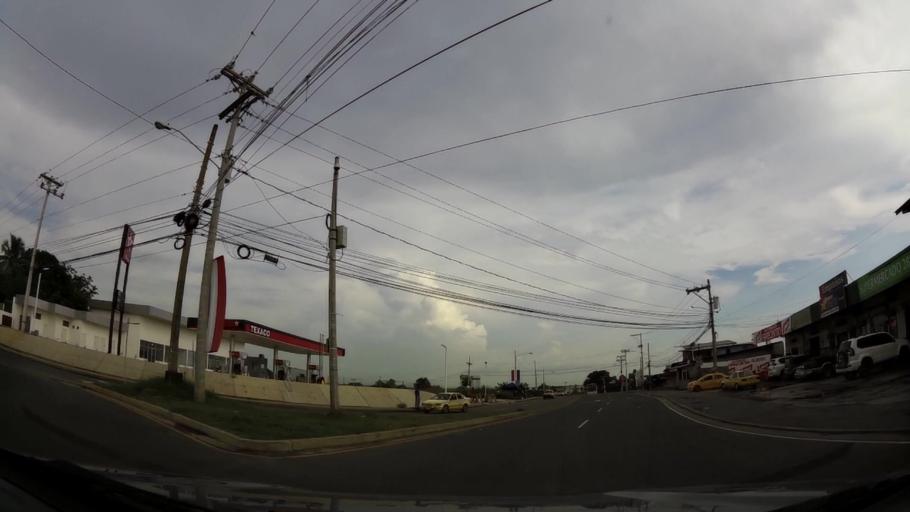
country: PA
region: Panama
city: Tocumen
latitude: 9.0792
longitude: -79.3676
